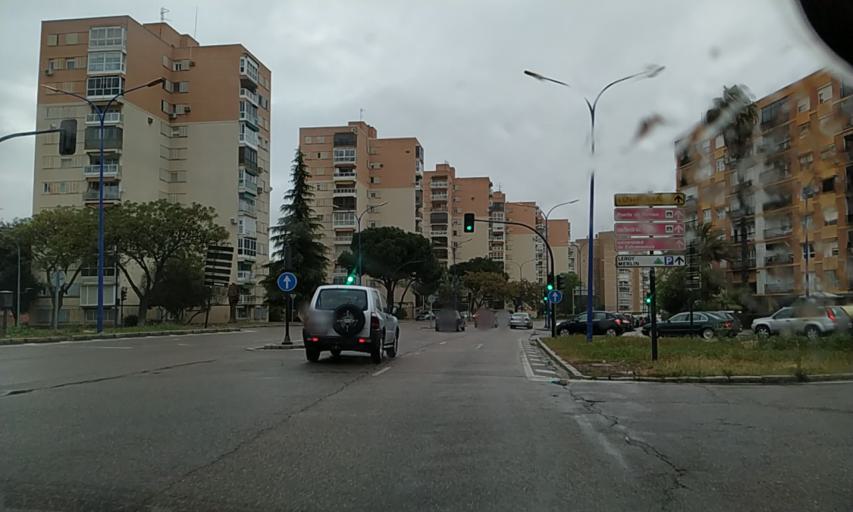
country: ES
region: Extremadura
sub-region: Provincia de Badajoz
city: Badajoz
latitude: 38.8730
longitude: -6.9808
